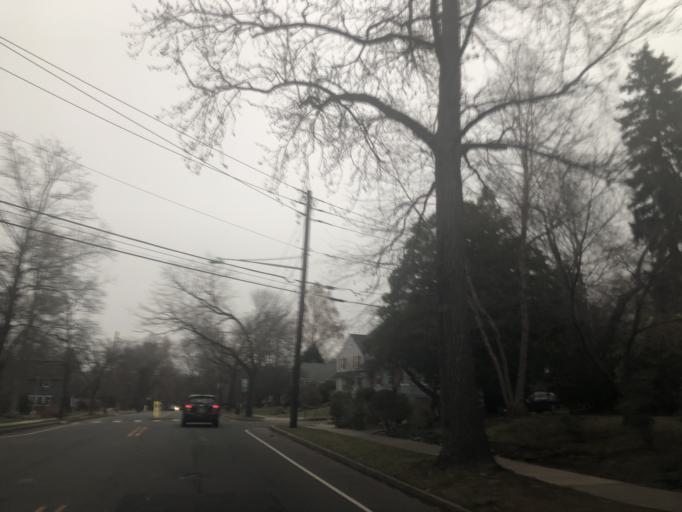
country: US
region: New Jersey
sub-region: Essex County
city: Maplewood
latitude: 40.7303
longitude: -74.2661
